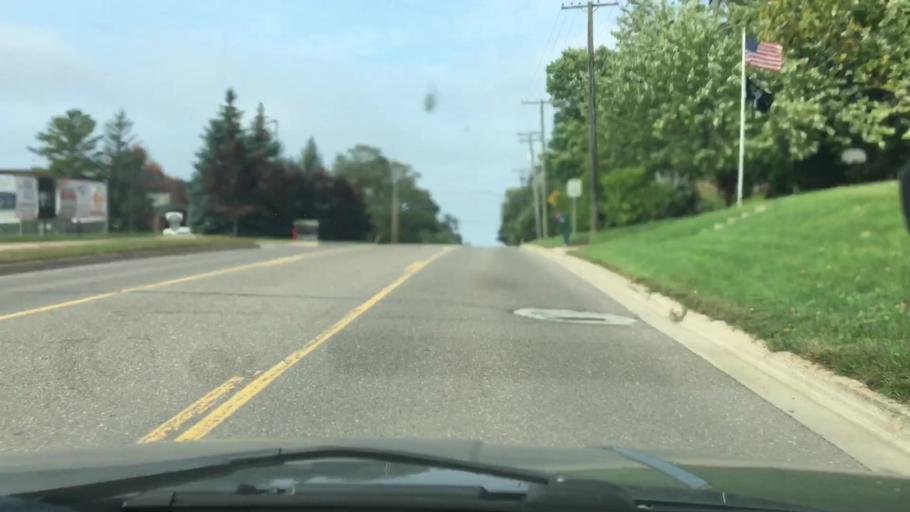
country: US
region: Michigan
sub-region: Livingston County
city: Brighton
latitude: 42.5298
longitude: -83.7744
